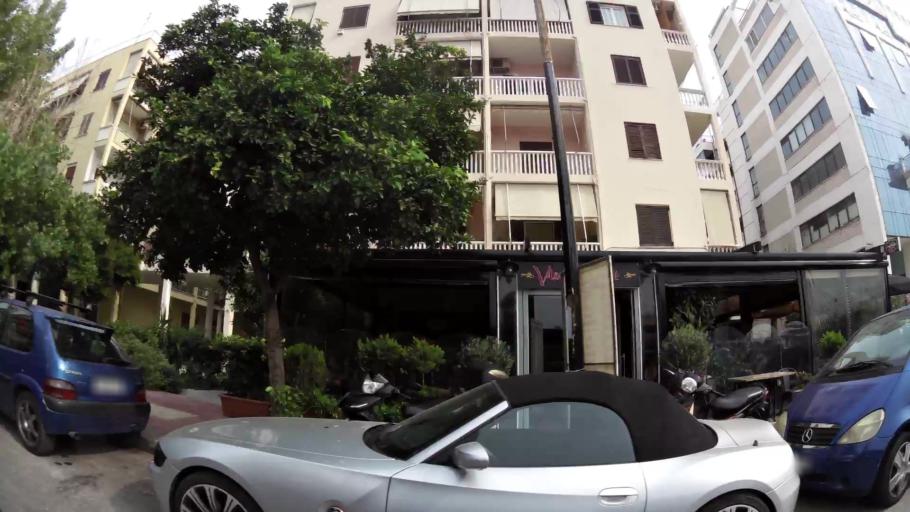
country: GR
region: Attica
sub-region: Nomarchia Athinas
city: Moskhaton
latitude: 37.9453
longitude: 23.6692
